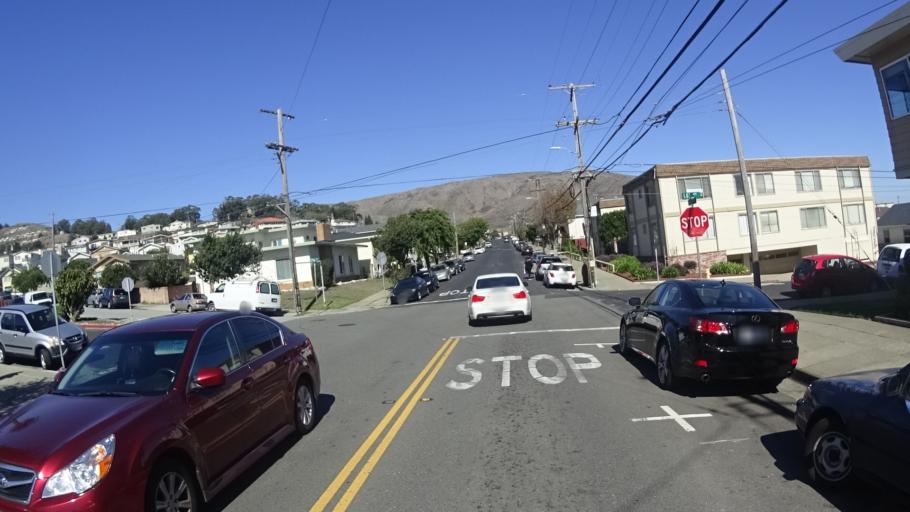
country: US
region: California
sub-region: San Mateo County
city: South San Francisco
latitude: 37.6574
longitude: -122.4118
